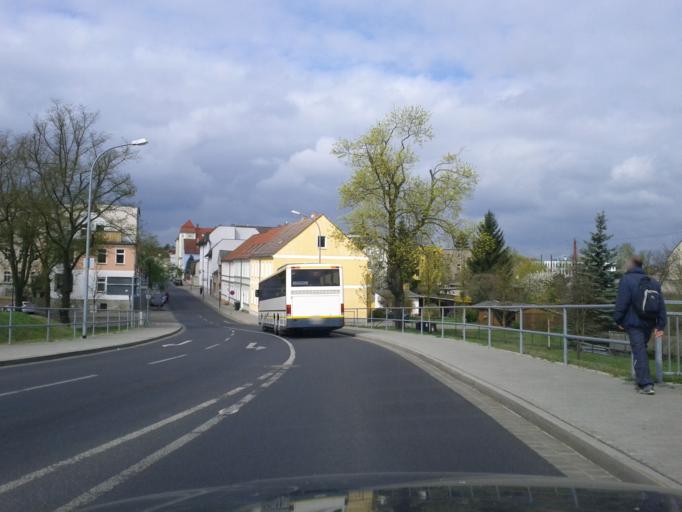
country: DE
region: Brandenburg
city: Furstenwalde
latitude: 52.3647
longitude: 14.0669
